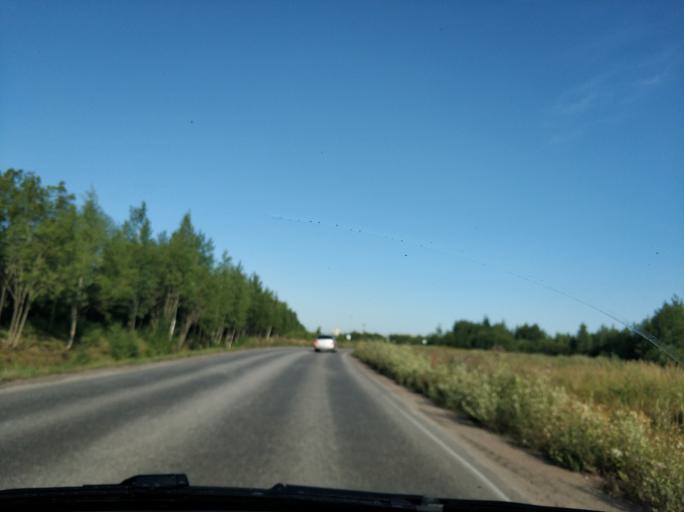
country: RU
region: St.-Petersburg
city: Grazhdanka
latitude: 60.0491
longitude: 30.4051
